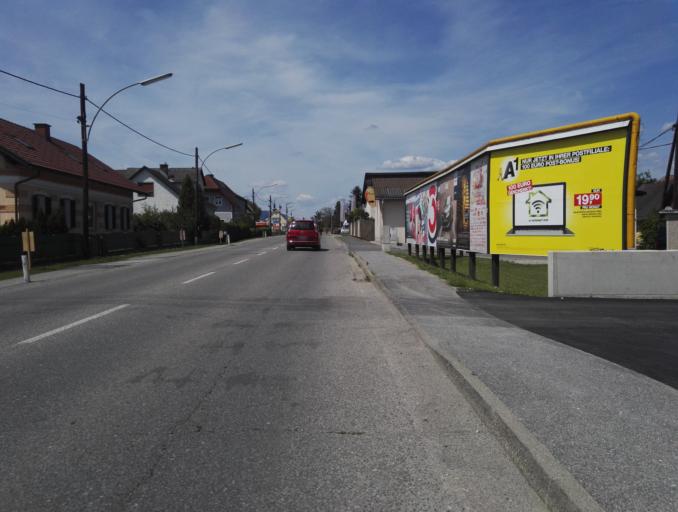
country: AT
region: Styria
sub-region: Politischer Bezirk Graz-Umgebung
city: Feldkirchen bei Graz
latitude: 47.0071
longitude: 15.4464
